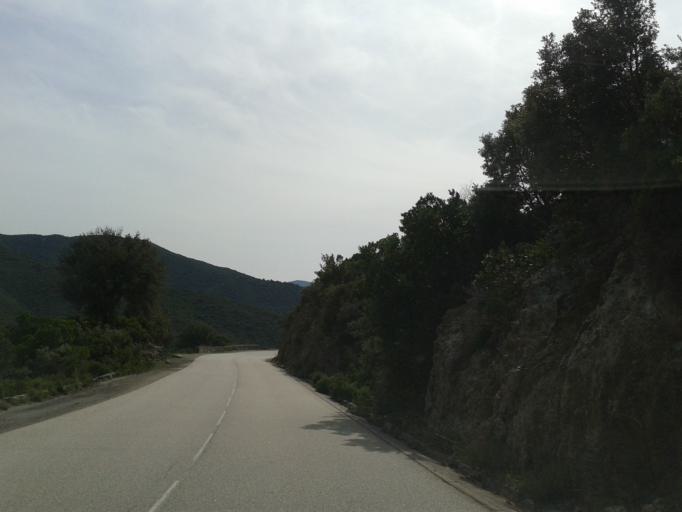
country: FR
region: Corsica
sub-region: Departement de la Haute-Corse
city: Monticello
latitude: 42.6592
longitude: 9.1215
